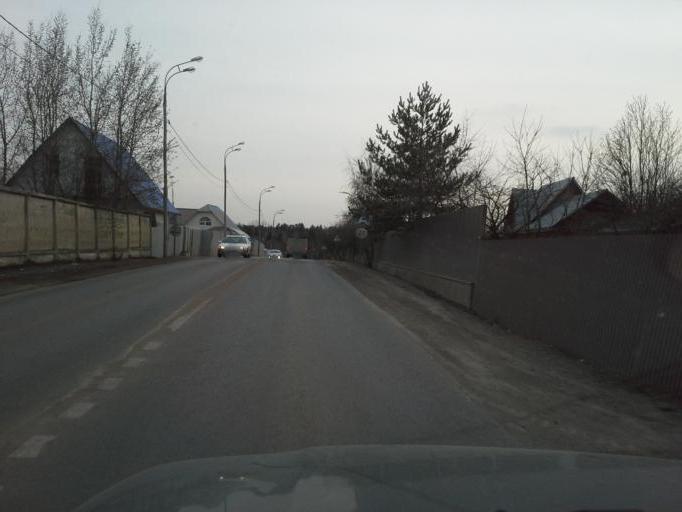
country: RU
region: Moskovskaya
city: Lesnoy Gorodok
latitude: 55.6503
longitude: 37.2113
